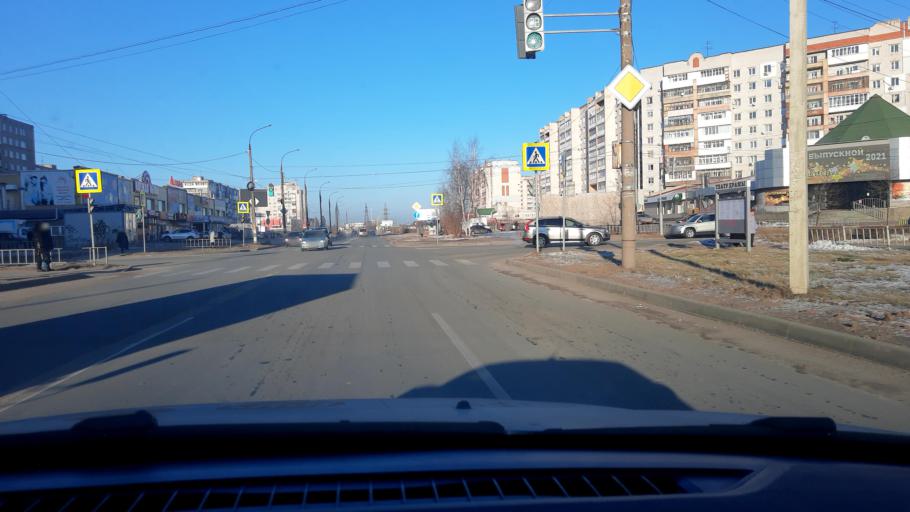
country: RU
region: Nizjnij Novgorod
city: Dzerzhinsk
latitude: 56.2305
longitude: 43.4110
